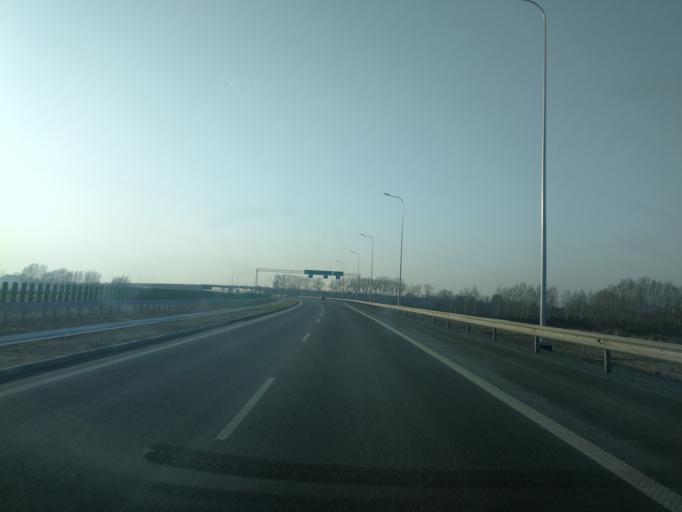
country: PL
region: Warmian-Masurian Voivodeship
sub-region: Powiat elblaski
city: Elblag
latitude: 54.1625
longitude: 19.3533
